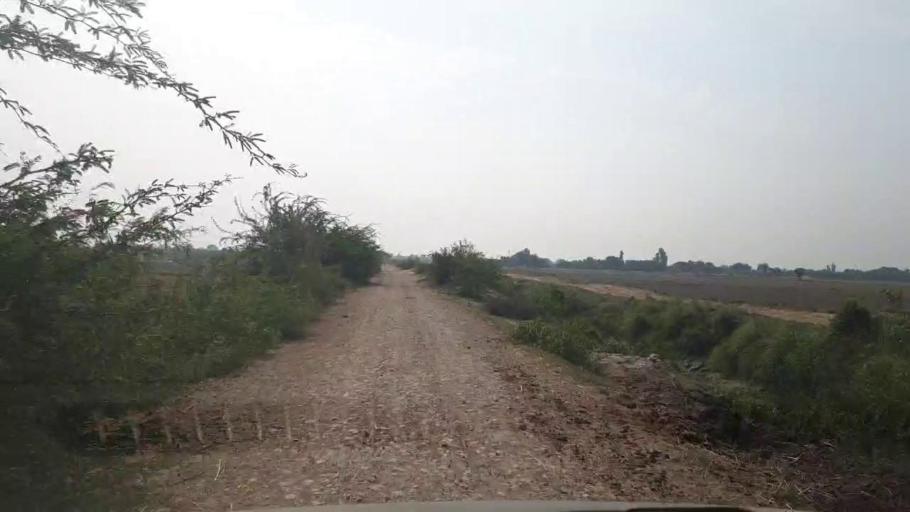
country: PK
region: Sindh
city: Tando Muhammad Khan
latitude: 25.1221
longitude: 68.4923
